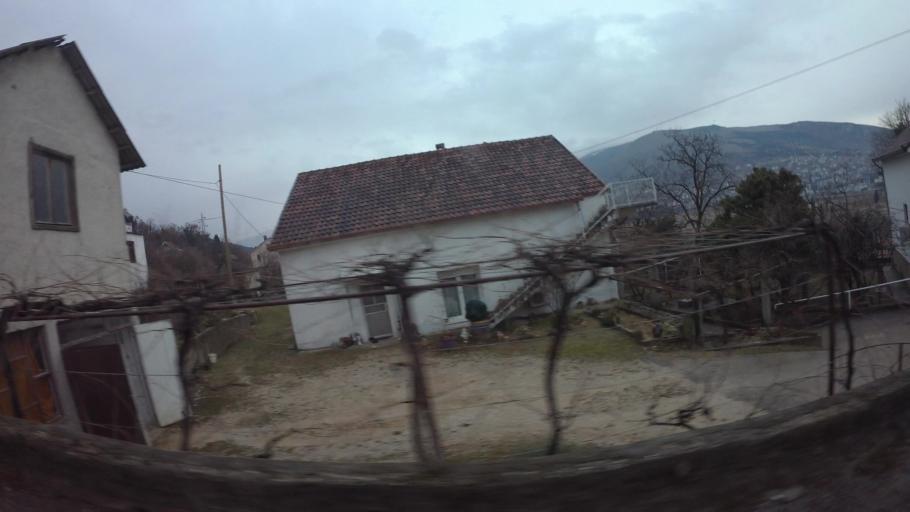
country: BA
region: Federation of Bosnia and Herzegovina
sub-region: Hercegovacko-Bosanski Kanton
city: Mostar
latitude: 43.3634
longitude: 17.8029
